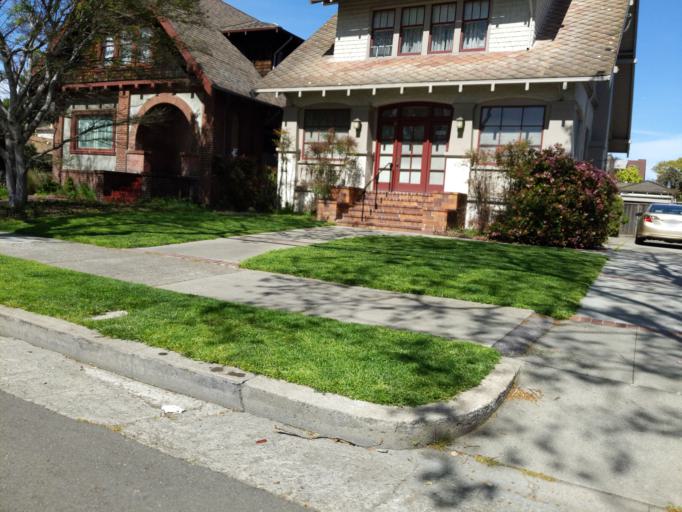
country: US
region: California
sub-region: Alameda County
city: Alameda
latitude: 37.7597
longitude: -122.2340
